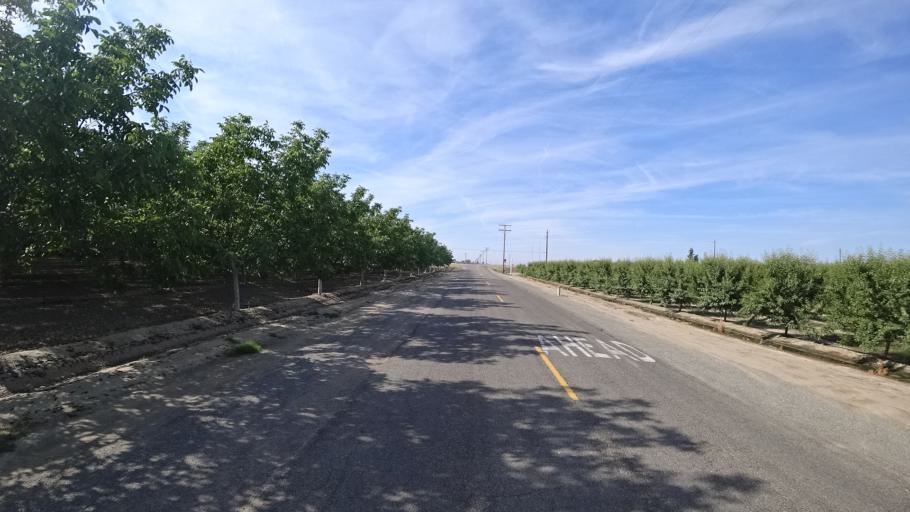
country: US
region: California
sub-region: Tulare County
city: Goshen
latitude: 36.3298
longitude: -119.4931
